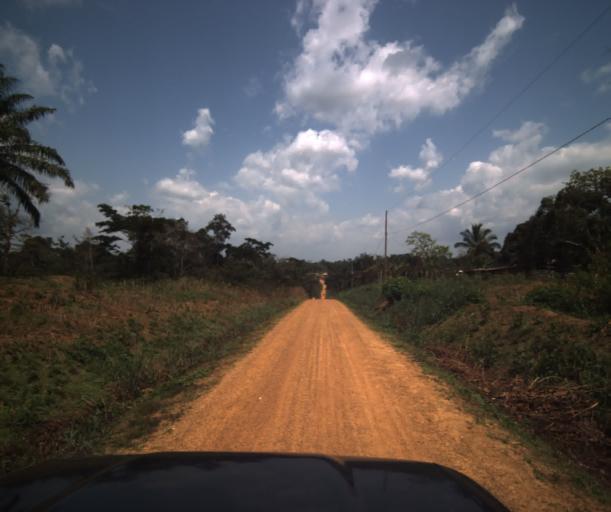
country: CM
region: Centre
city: Eseka
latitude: 3.5407
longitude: 11.0156
